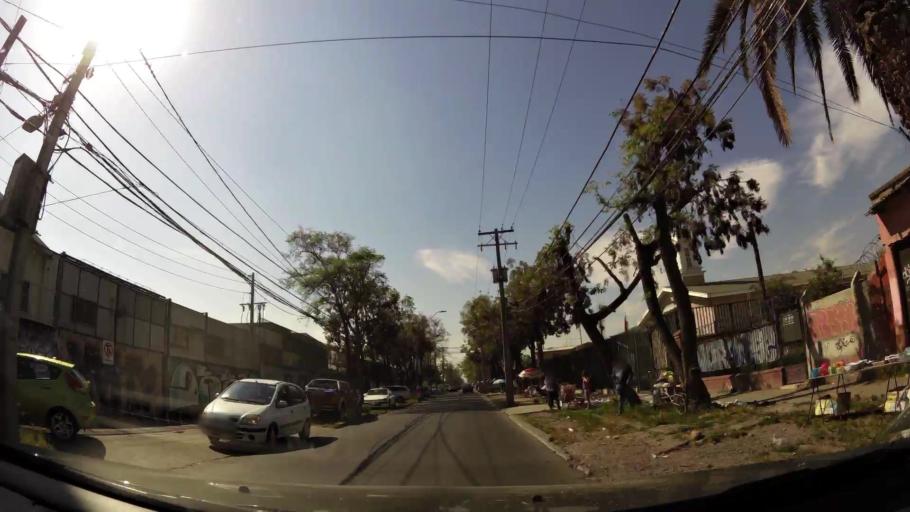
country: CL
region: Santiago Metropolitan
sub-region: Provincia de Maipo
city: San Bernardo
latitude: -33.5952
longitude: -70.6940
